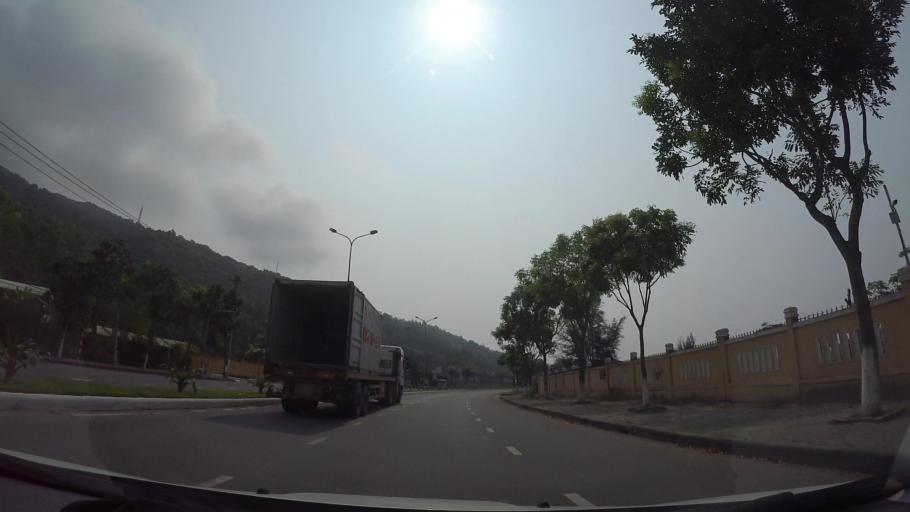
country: VN
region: Da Nang
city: Da Nang
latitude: 16.1136
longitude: 108.2431
